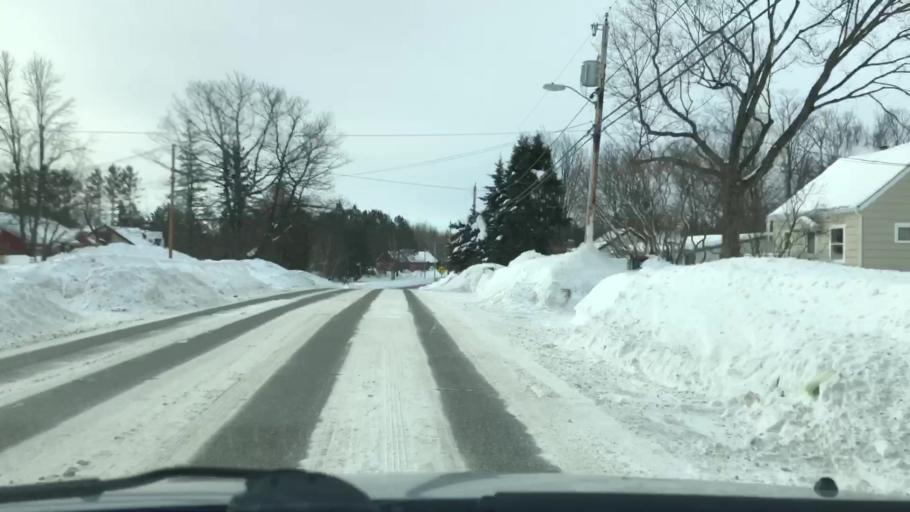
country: US
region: Minnesota
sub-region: Saint Louis County
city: Duluth
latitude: 46.7956
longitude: -92.1494
